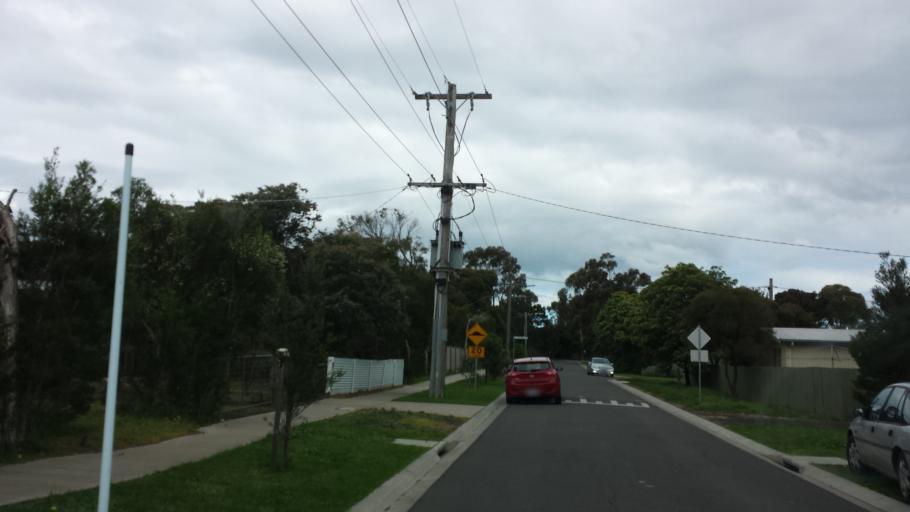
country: AU
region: Victoria
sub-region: Bass Coast
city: Cowes
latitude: -38.4579
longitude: 145.2149
